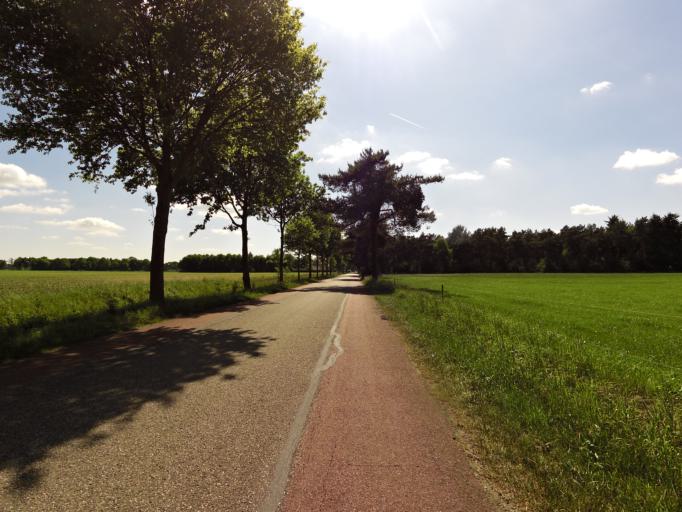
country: NL
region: Gelderland
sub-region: Gemeente Bronckhorst
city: Zelhem
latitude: 52.0358
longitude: 6.3562
